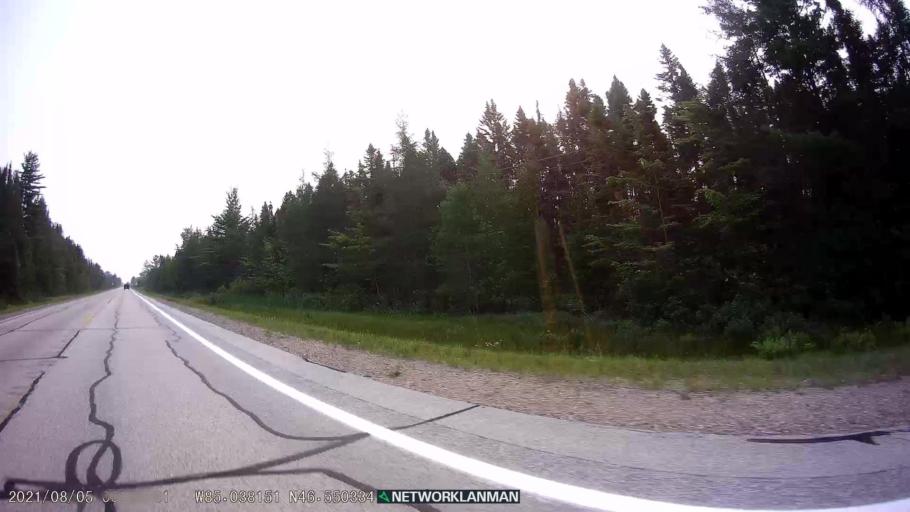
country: US
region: Michigan
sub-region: Luce County
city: Newberry
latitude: 46.5501
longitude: -85.0388
